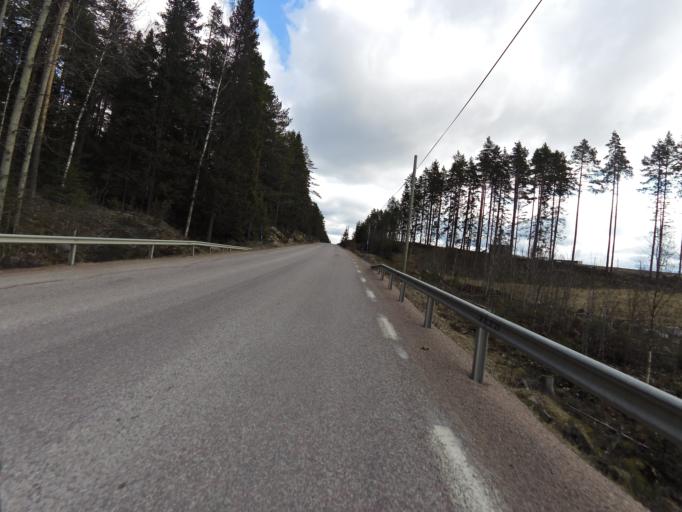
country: SE
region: Dalarna
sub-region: Hedemora Kommun
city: Brunna
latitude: 60.3125
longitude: 16.1513
